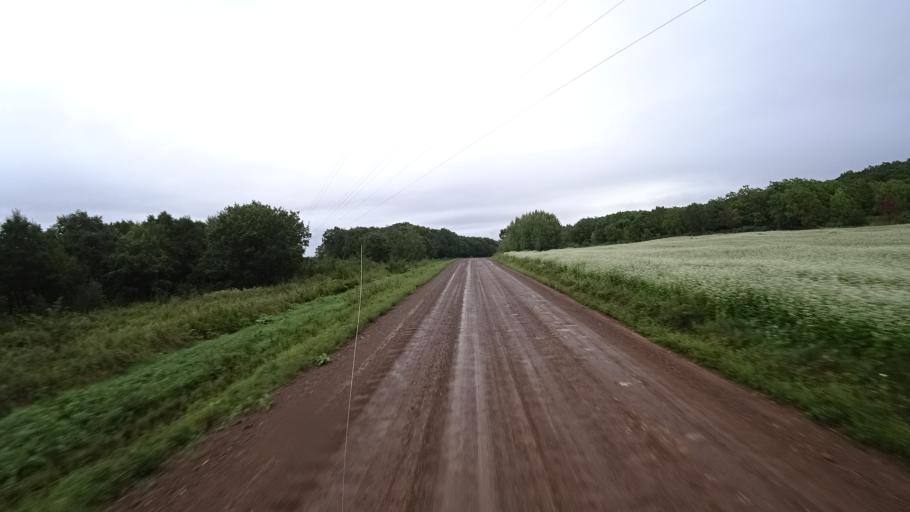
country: RU
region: Primorskiy
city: Monastyrishche
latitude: 44.2743
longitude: 132.4437
